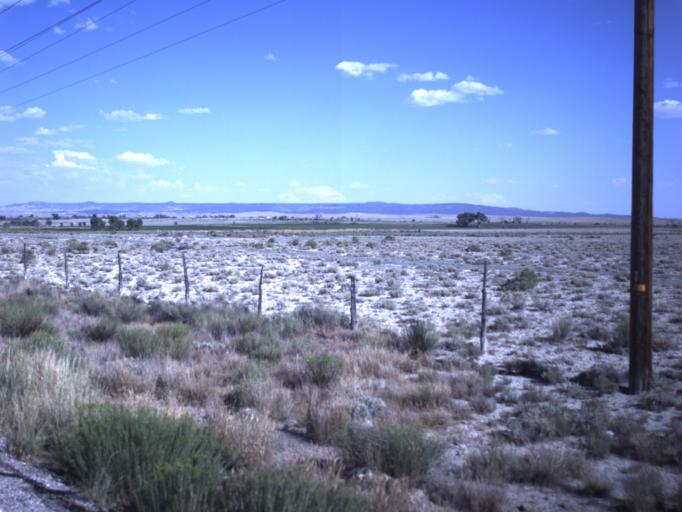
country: US
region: Utah
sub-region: Emery County
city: Huntington
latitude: 39.3450
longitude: -110.9063
